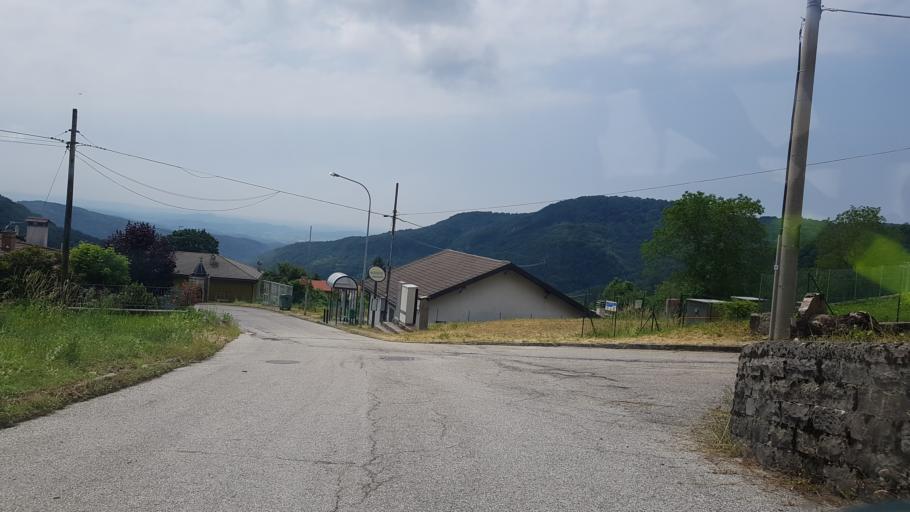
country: IT
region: Friuli Venezia Giulia
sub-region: Provincia di Udine
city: Torreano
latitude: 46.1726
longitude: 13.4306
